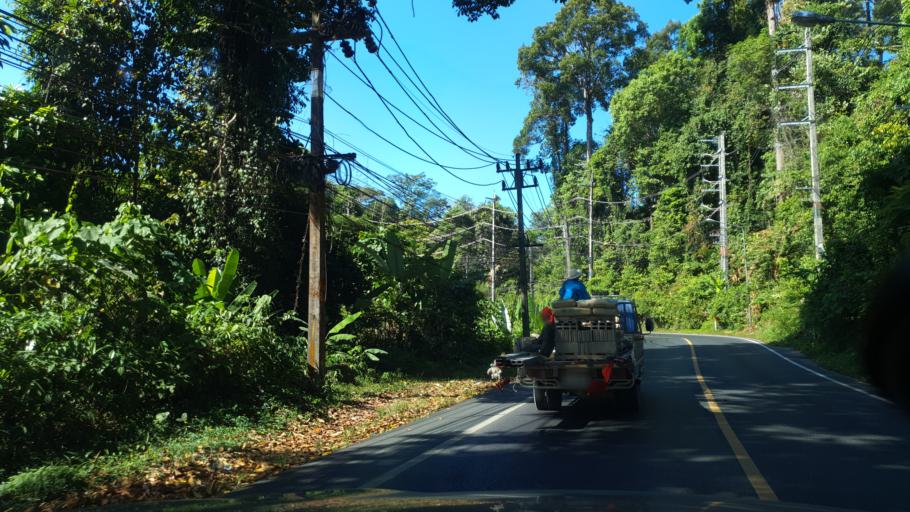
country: TH
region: Phangnga
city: Ban Khao Lak
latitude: 8.6202
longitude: 98.2390
